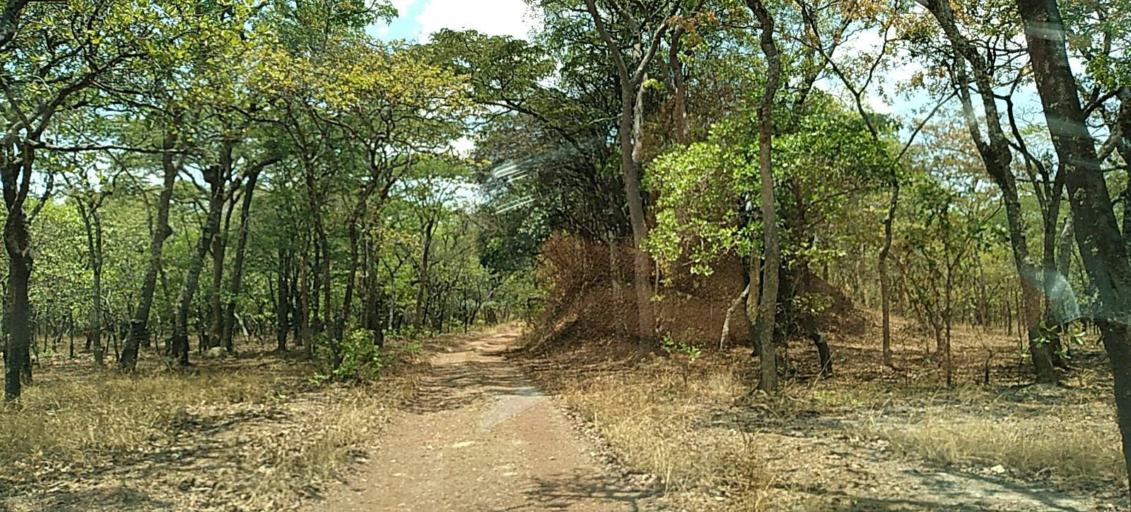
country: ZM
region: Copperbelt
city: Chililabombwe
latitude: -12.4583
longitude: 27.6984
